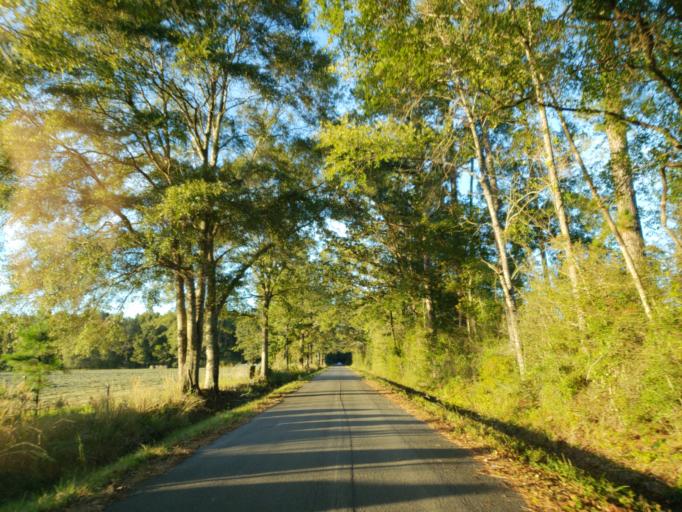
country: US
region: Mississippi
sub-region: Wayne County
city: Belmont
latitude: 31.4375
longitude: -88.5264
